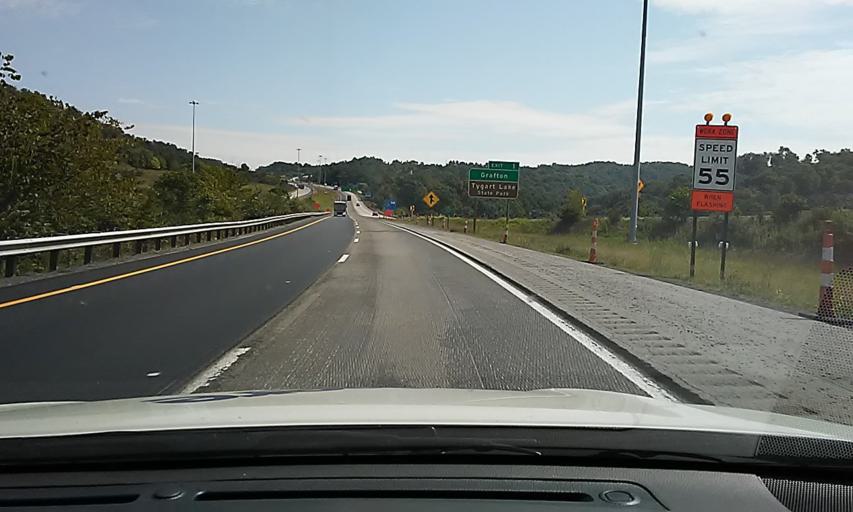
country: US
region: West Virginia
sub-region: Monongalia County
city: Morgantown
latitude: 39.5785
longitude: -79.9752
